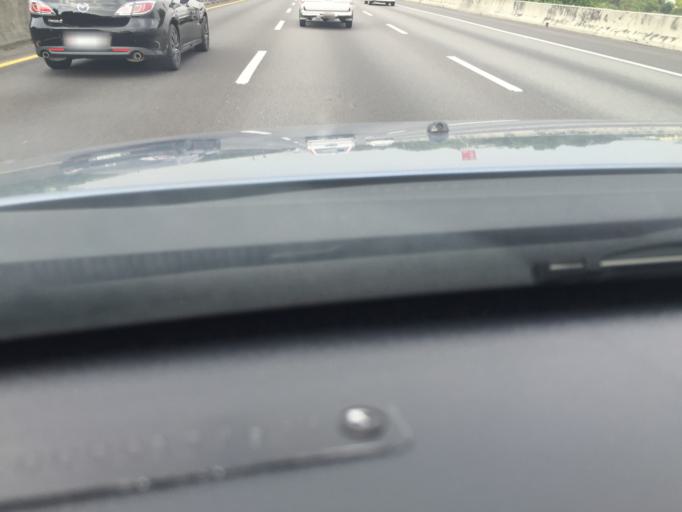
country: TW
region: Taiwan
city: Fengyuan
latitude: 24.2343
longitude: 120.6876
